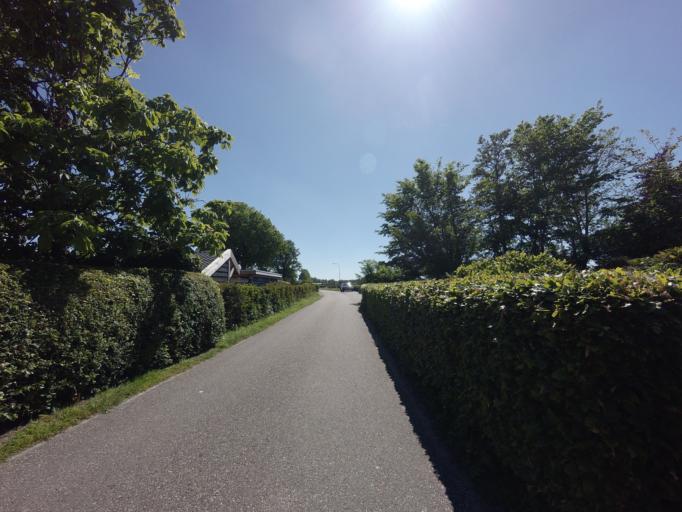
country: NL
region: North Holland
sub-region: Gemeente Uitgeest
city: Uitgeest
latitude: 52.5476
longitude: 4.7262
